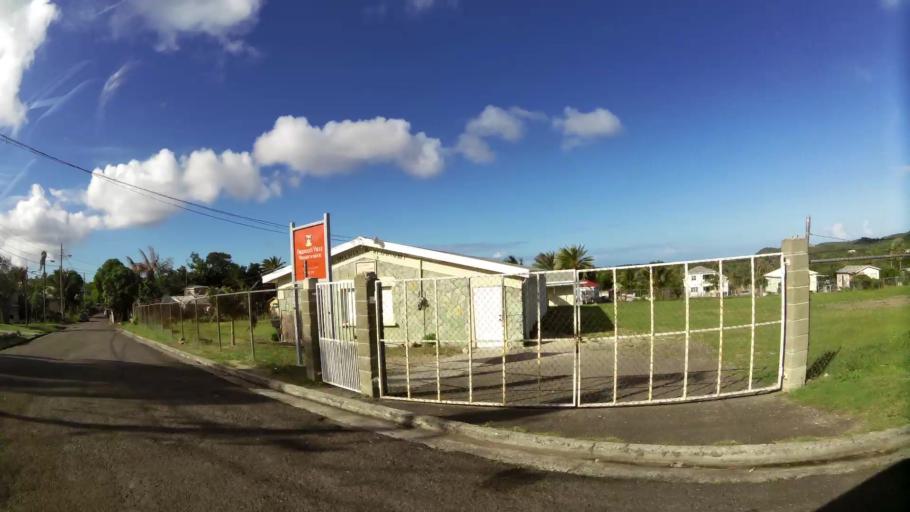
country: AG
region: Saint Peter
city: All Saints
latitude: 17.0801
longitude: -61.7855
